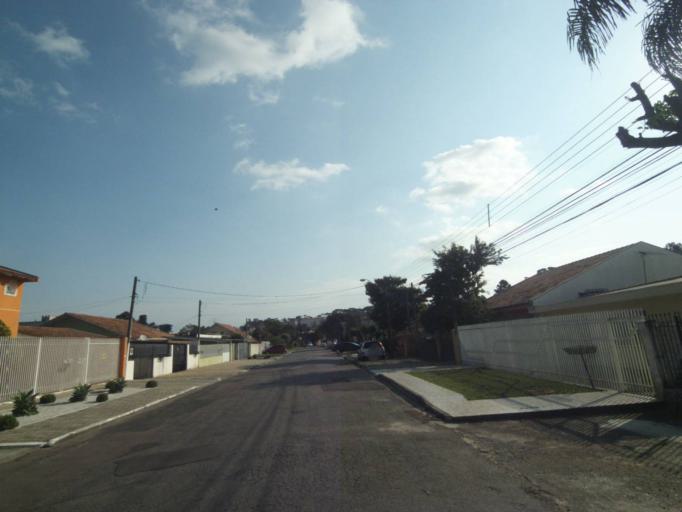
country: BR
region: Parana
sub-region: Curitiba
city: Curitiba
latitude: -25.4842
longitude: -49.3353
